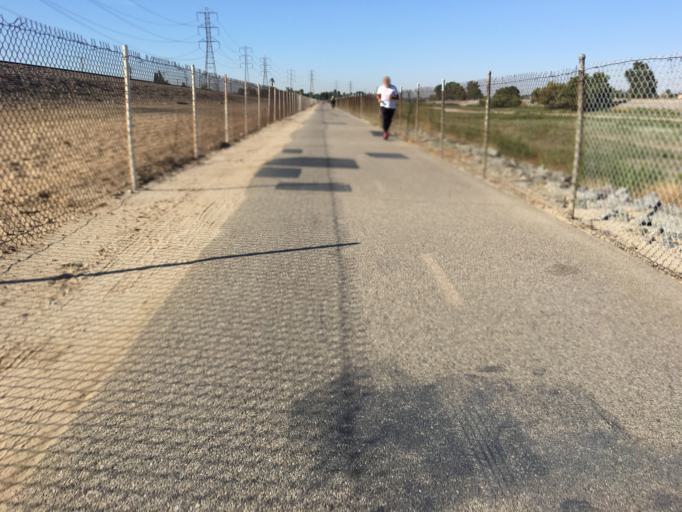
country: US
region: California
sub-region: Los Angeles County
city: West Whittier-Los Nietos
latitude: 33.9895
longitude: -118.0742
